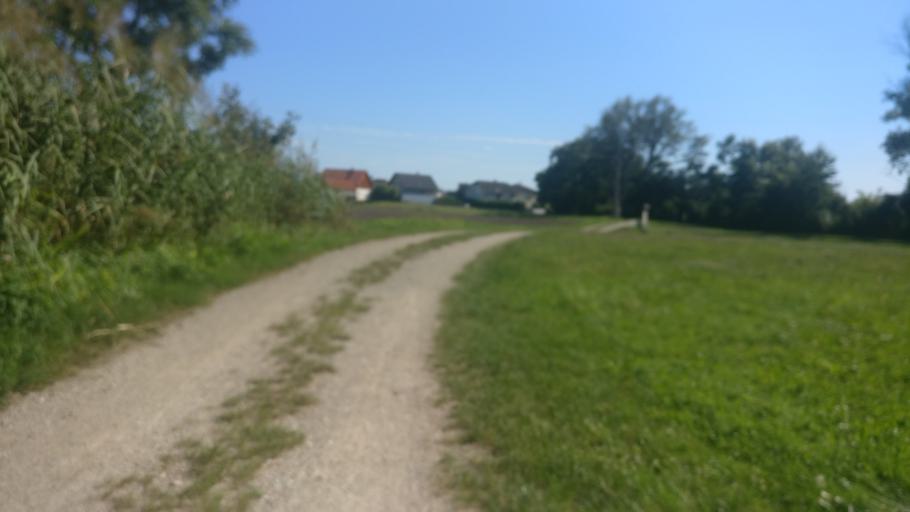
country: AT
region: Lower Austria
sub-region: Politischer Bezirk Baden
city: Mitterndorf an der Fischa
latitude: 47.9701
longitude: 16.4393
